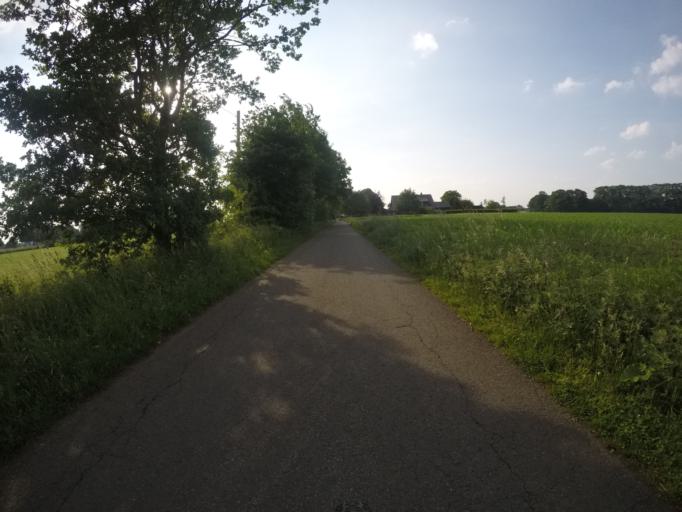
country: DE
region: North Rhine-Westphalia
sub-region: Regierungsbezirk Munster
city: Isselburg
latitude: 51.8393
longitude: 6.4819
